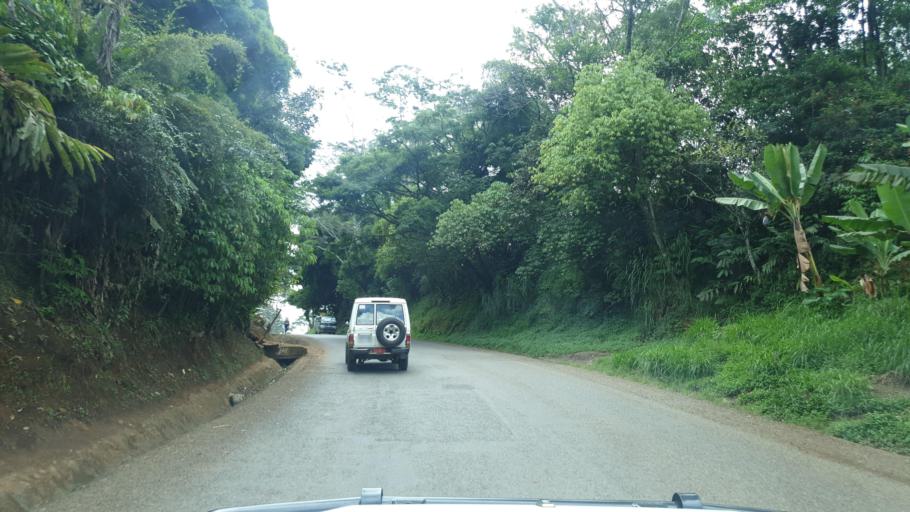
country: PG
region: Eastern Highlands
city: Goroka
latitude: -6.0422
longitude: 145.3729
